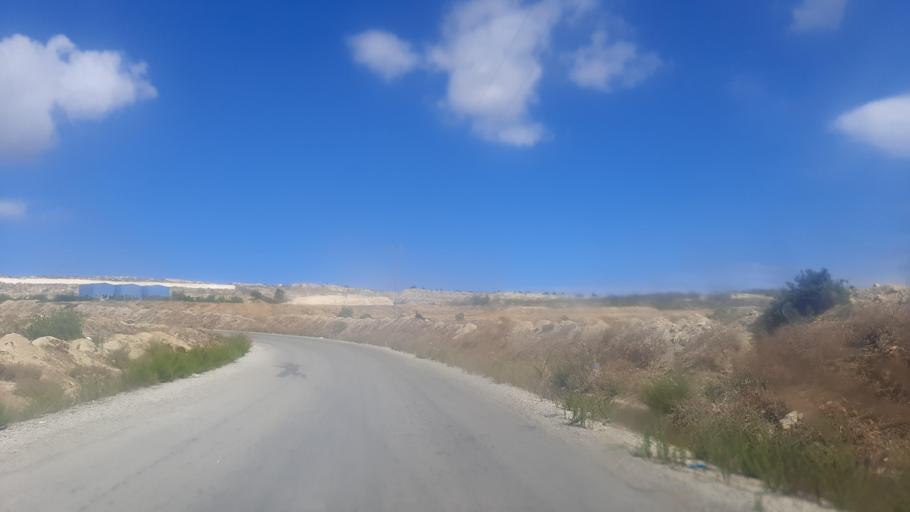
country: TN
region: Nabul
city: Nabeul
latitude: 36.4912
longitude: 10.7056
